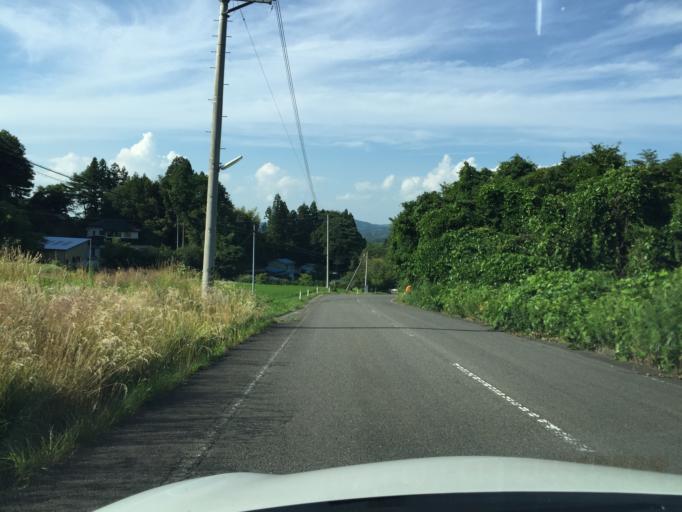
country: JP
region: Fukushima
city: Sukagawa
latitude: 37.2712
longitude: 140.5020
